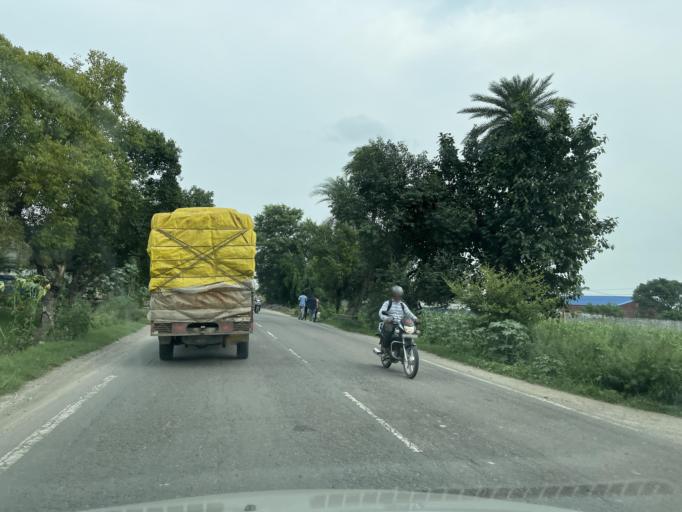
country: IN
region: Uttar Pradesh
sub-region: Rampur
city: Bilaspur
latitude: 29.0335
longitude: 79.2591
